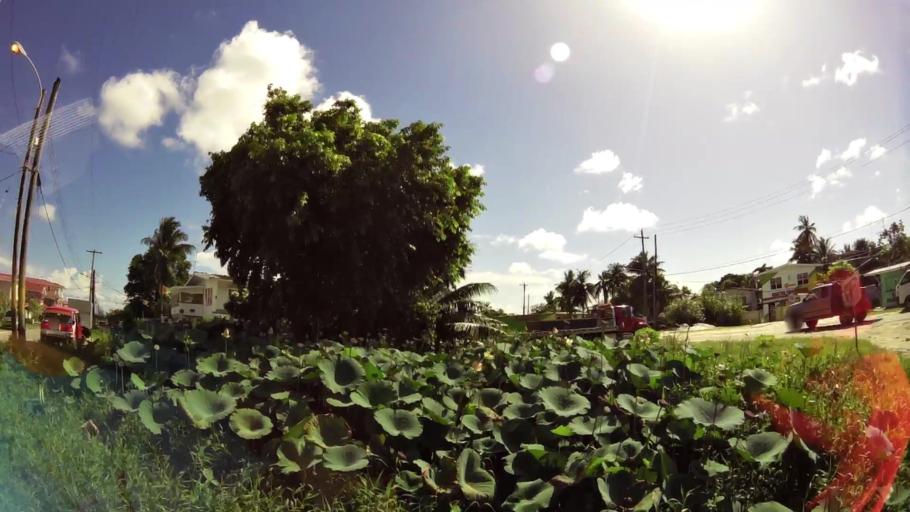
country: GY
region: Demerara-Mahaica
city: Georgetown
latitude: 6.8197
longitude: -58.1357
